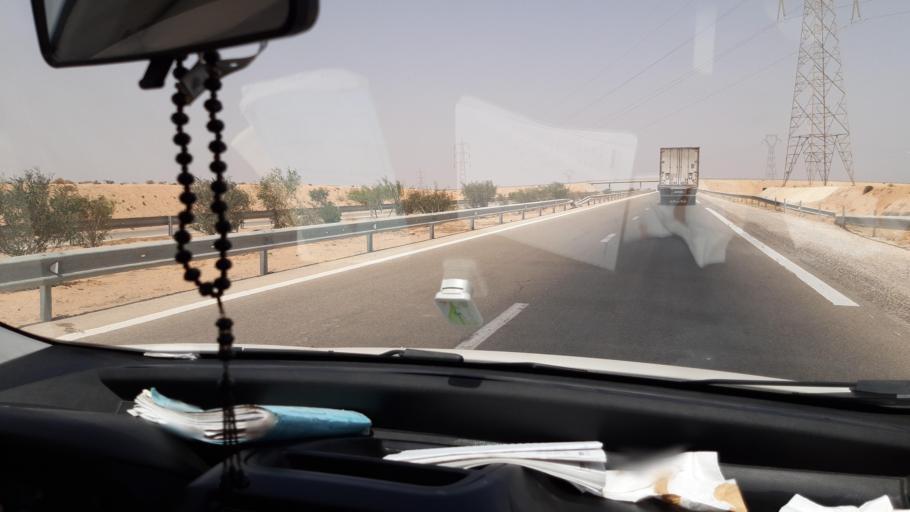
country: TN
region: Safaqis
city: Skhira
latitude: 34.1521
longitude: 9.9686
